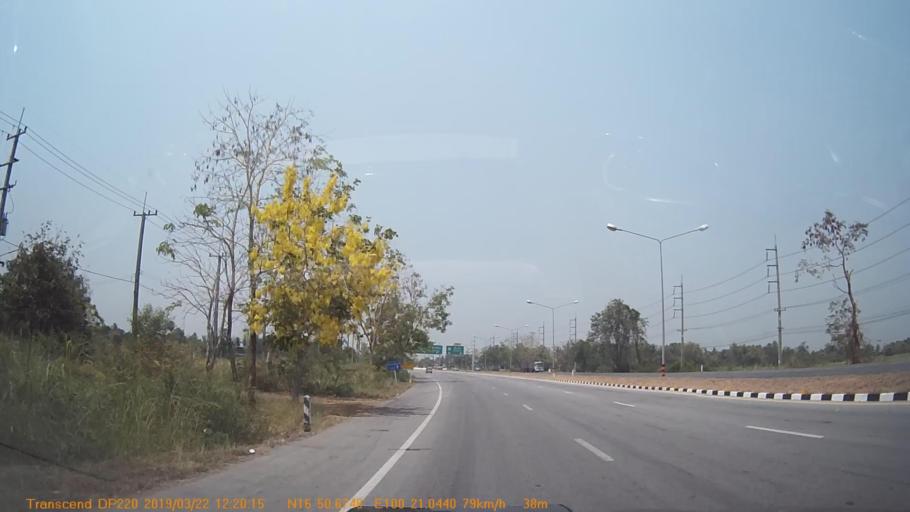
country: TH
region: Phitsanulok
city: Wang Thong
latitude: 16.8449
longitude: 100.3503
